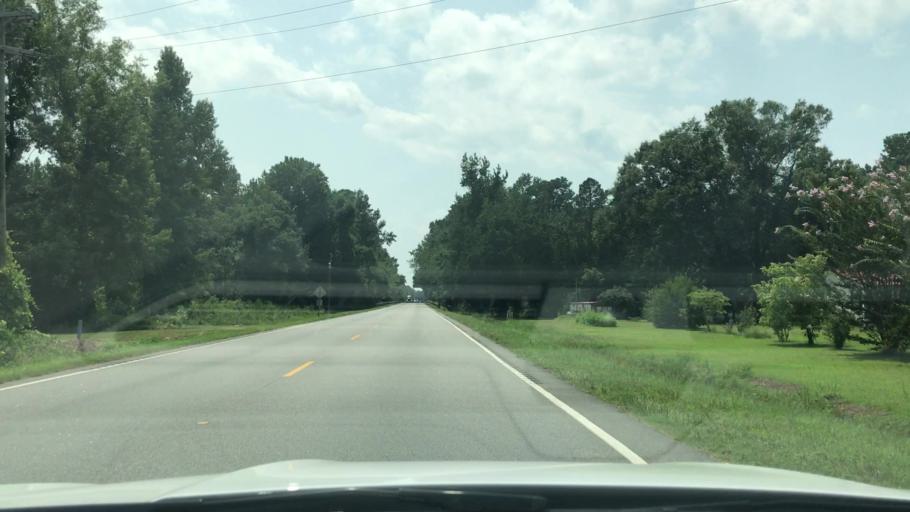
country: US
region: South Carolina
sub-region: Horry County
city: Socastee
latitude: 33.6891
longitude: -79.1194
